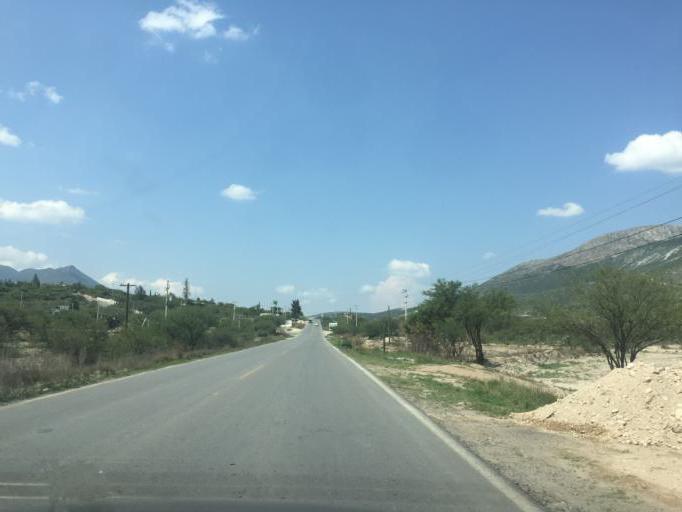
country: MX
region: Hidalgo
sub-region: Ixmiquilpan
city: El Nith
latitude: 20.5832
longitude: -99.1313
